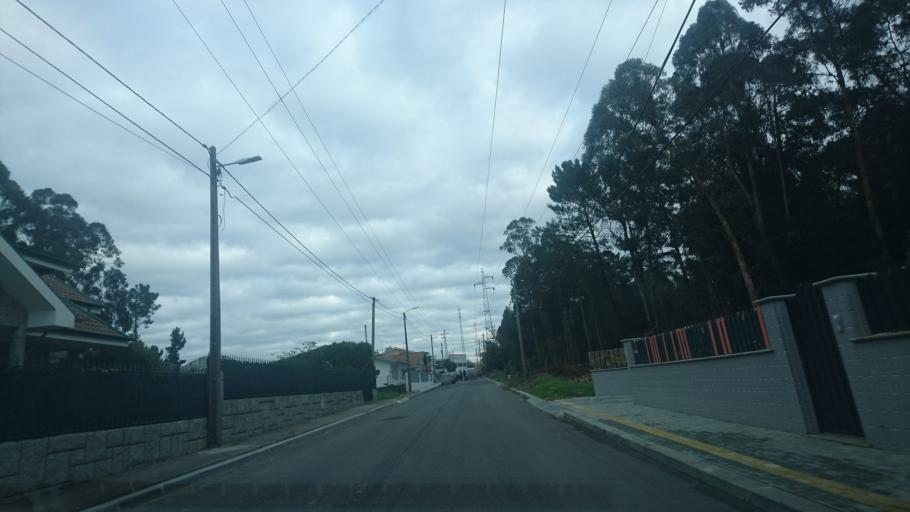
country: PT
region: Aveiro
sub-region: Santa Maria da Feira
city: Rio Meao
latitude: 40.9582
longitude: -8.5987
